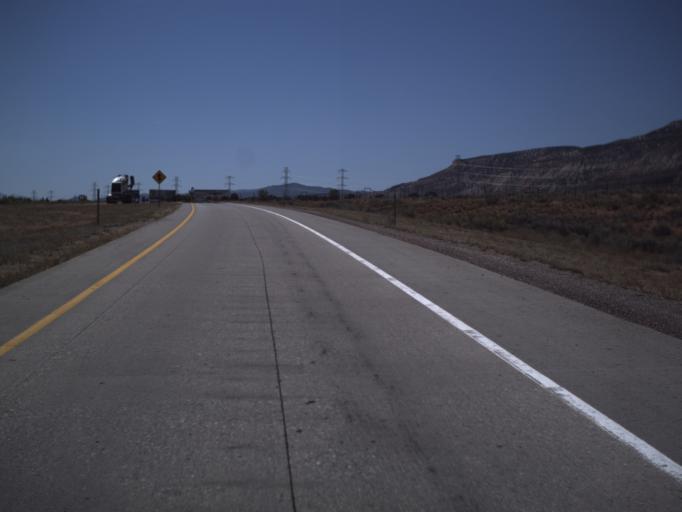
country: US
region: Utah
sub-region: Sevier County
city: Aurora
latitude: 38.8726
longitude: -111.9700
